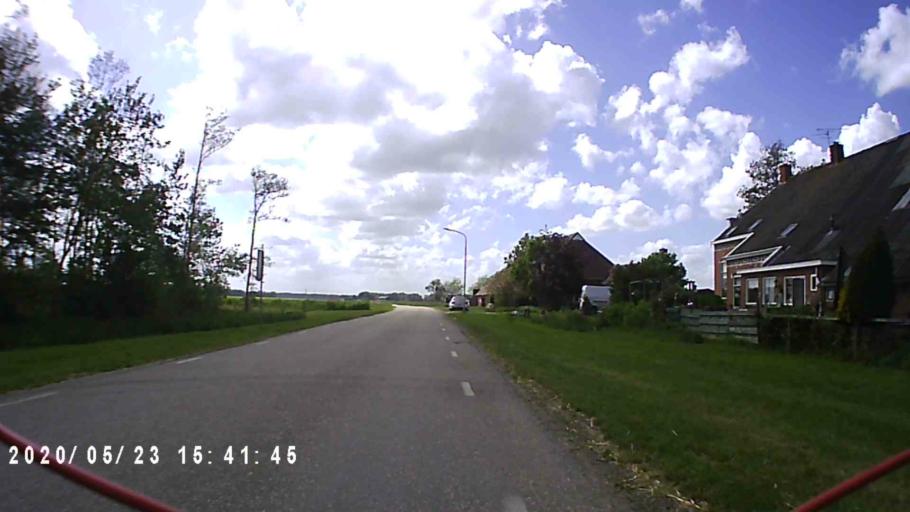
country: NL
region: Groningen
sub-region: Gemeente Delfzijl
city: Delfzijl
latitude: 53.2809
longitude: 6.9308
